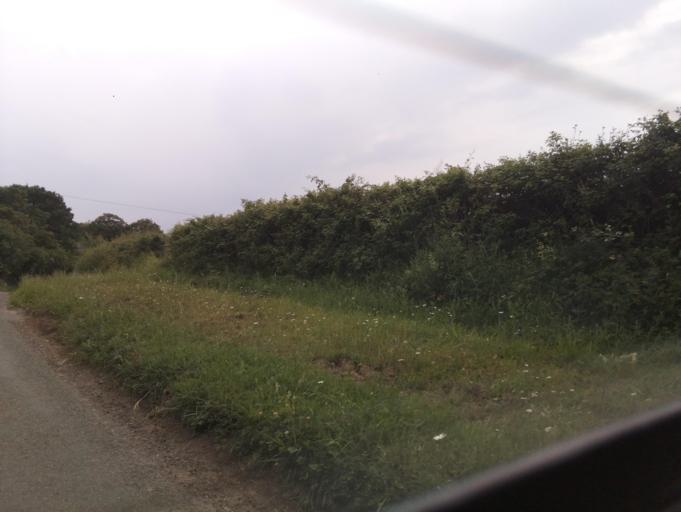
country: GB
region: England
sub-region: Devon
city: Colyton
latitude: 50.7280
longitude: -3.0457
